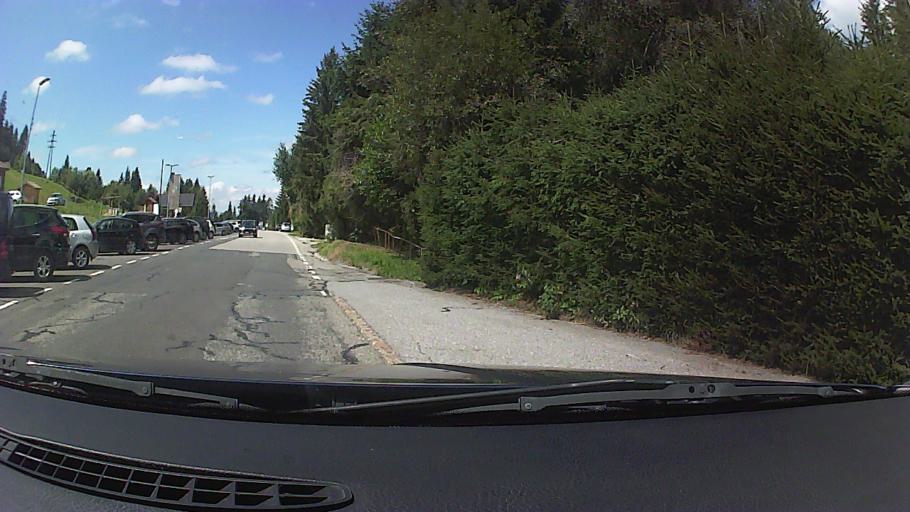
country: CH
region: Fribourg
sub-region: Veveyse District
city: Chatel-Saint-Denis
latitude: 46.5214
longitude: 6.9514
